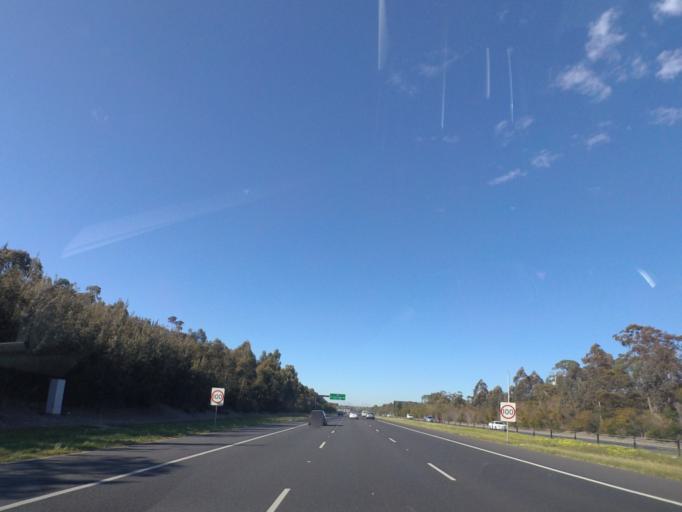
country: AU
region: Victoria
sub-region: Knox
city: Wantirna South
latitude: -37.8919
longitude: 145.2150
